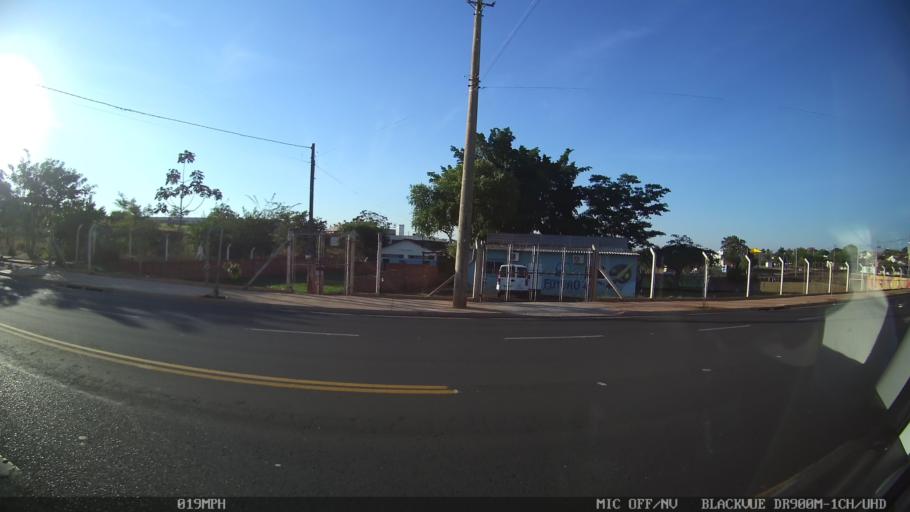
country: BR
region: Sao Paulo
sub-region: Sao Jose Do Rio Preto
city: Sao Jose do Rio Preto
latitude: -20.7916
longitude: -49.3499
